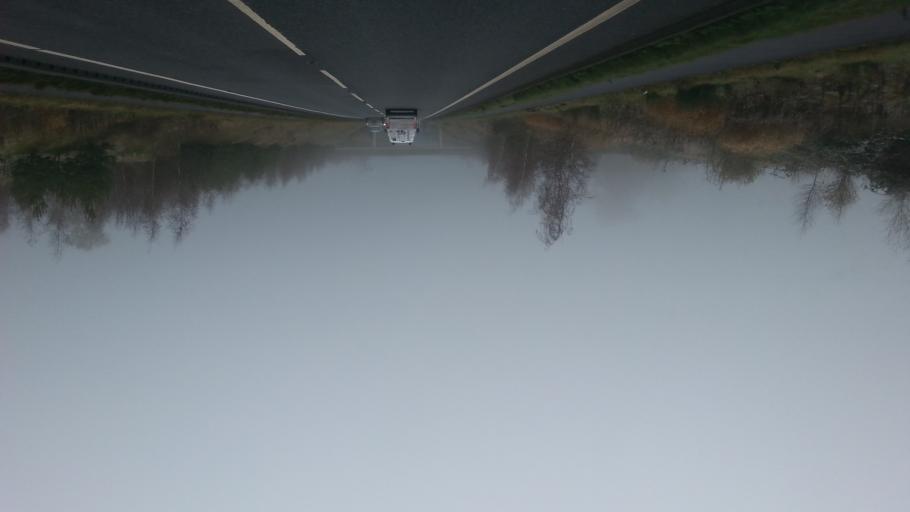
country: GB
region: England
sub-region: Cheshire East
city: Alderley Edge
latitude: 53.2826
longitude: -2.2470
